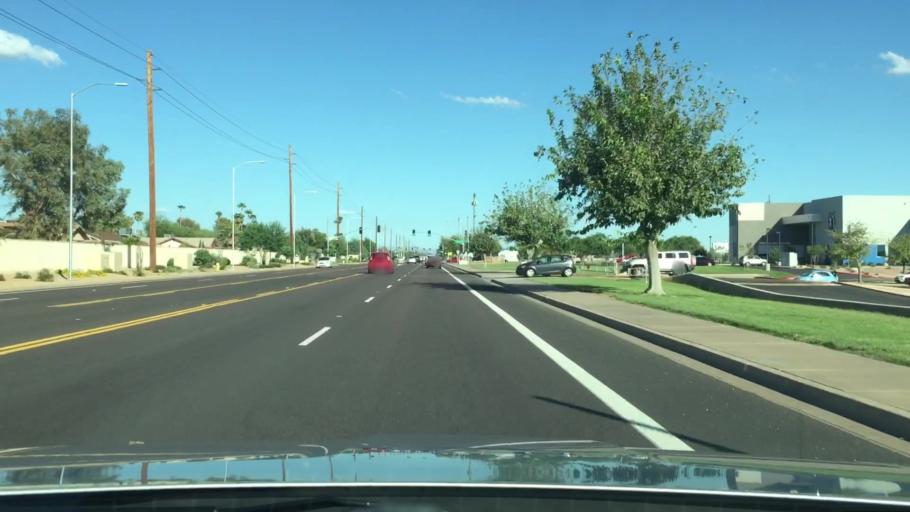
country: US
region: Arizona
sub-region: Maricopa County
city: San Carlos
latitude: 33.3641
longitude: -111.8698
